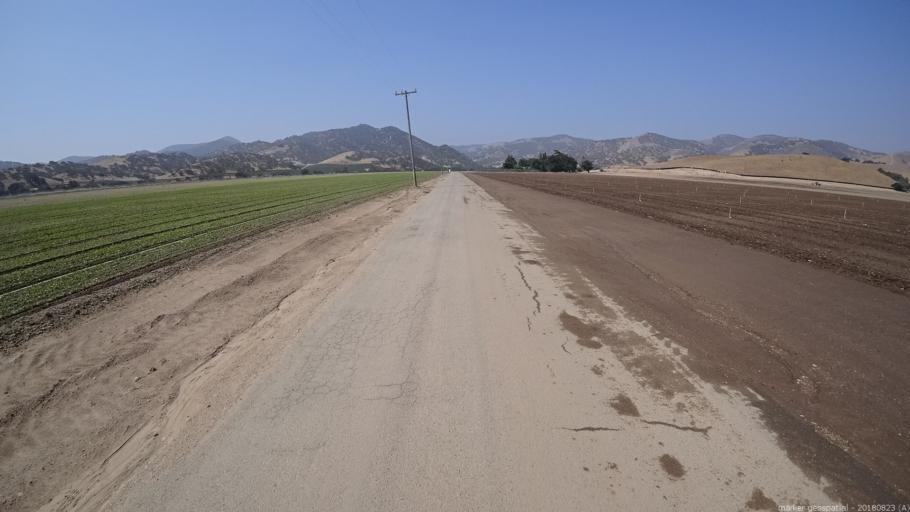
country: US
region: California
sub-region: Monterey County
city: King City
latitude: 36.2287
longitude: -121.1817
